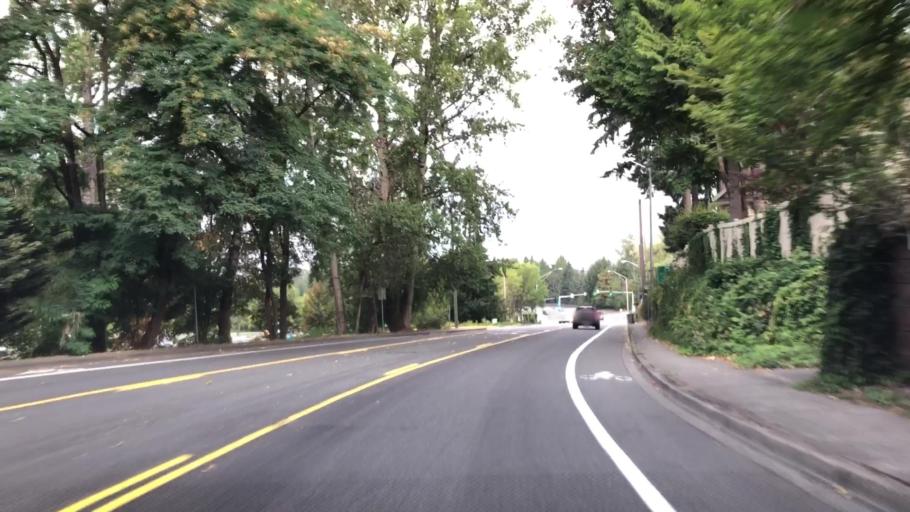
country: US
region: Washington
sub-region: King County
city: Kirkland
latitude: 47.6683
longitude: -122.1832
